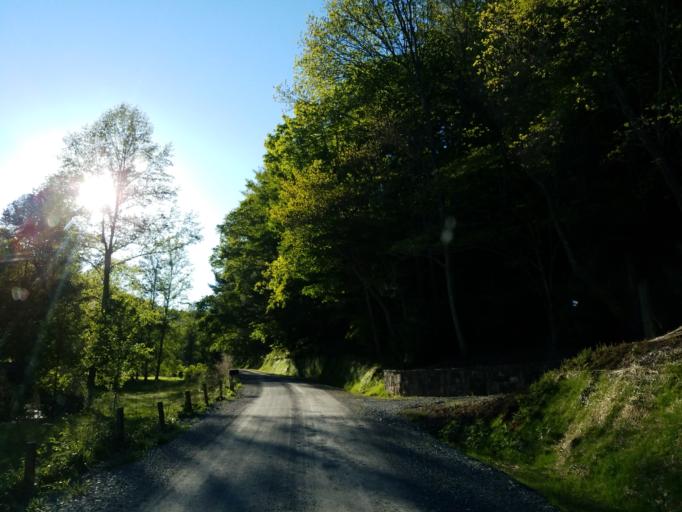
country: US
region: Georgia
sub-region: Fannin County
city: Blue Ridge
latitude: 34.7577
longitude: -84.2618
